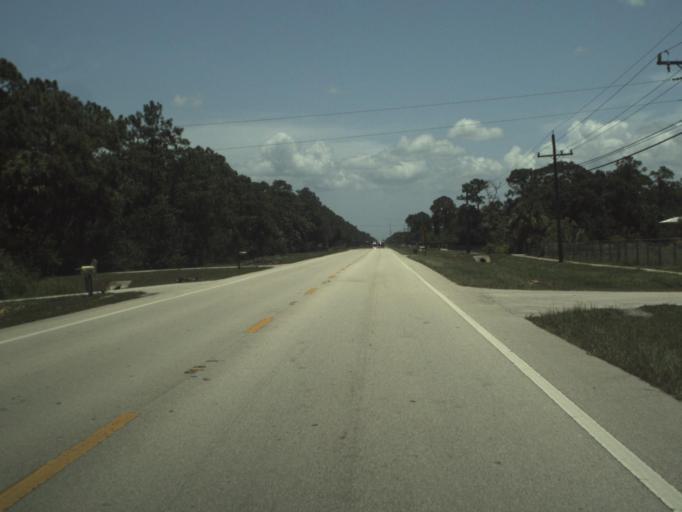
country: US
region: Florida
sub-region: Martin County
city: Palm City
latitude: 27.1617
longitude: -80.3576
